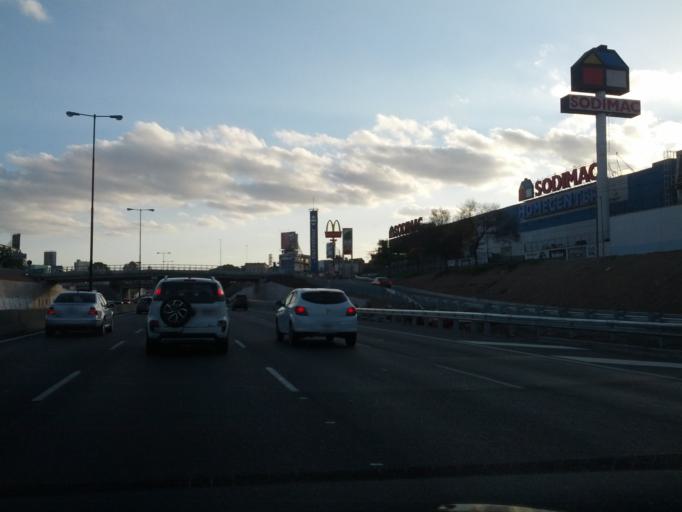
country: AR
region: Buenos Aires
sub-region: Partido de General San Martin
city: General San Martin
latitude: -34.5870
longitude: -58.5176
